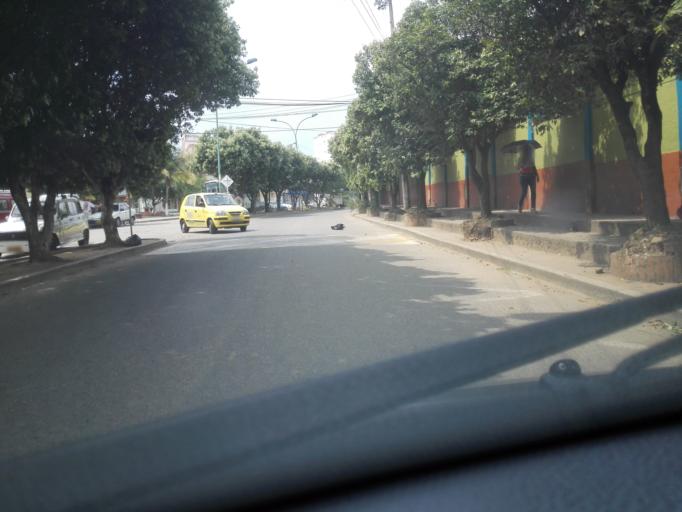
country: CO
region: Santander
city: Floridablanca
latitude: 7.0805
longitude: -73.1235
